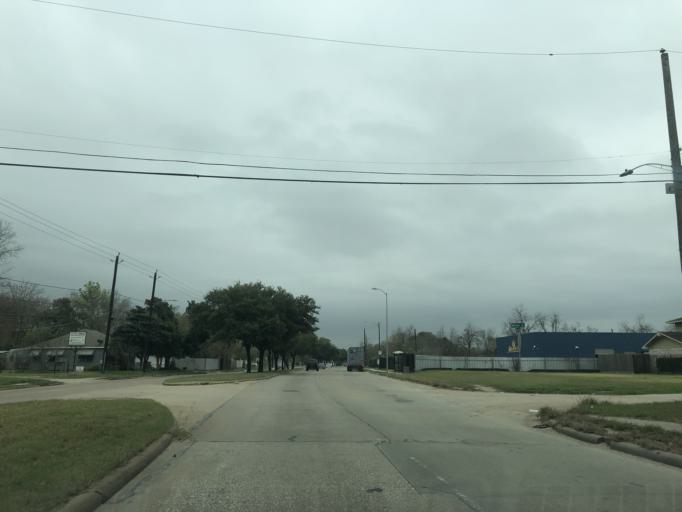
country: US
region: Texas
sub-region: Harris County
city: Jacinto City
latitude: 29.8235
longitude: -95.2845
